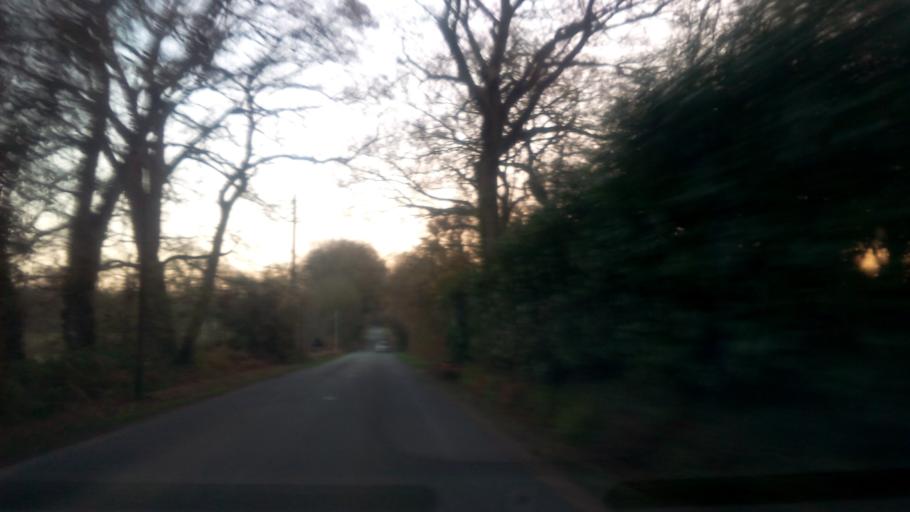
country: FR
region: Brittany
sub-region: Departement d'Ille-et-Vilaine
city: Bains-sur-Oust
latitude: 47.7161
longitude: -2.0538
